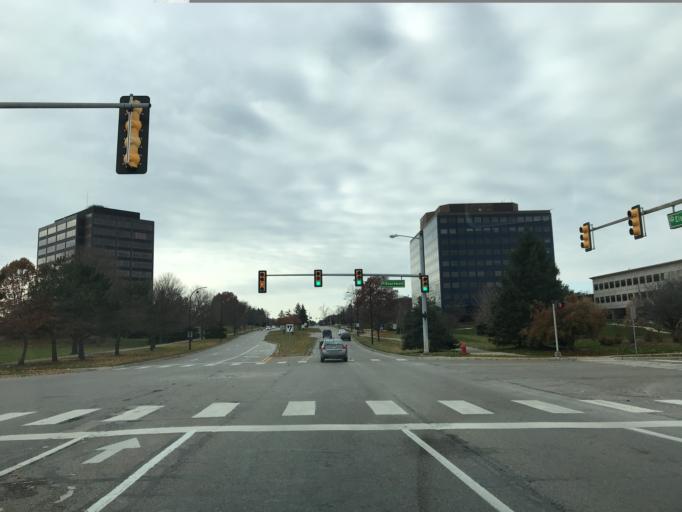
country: US
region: Michigan
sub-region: Washtenaw County
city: Ann Arbor
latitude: 42.2442
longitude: -83.7342
